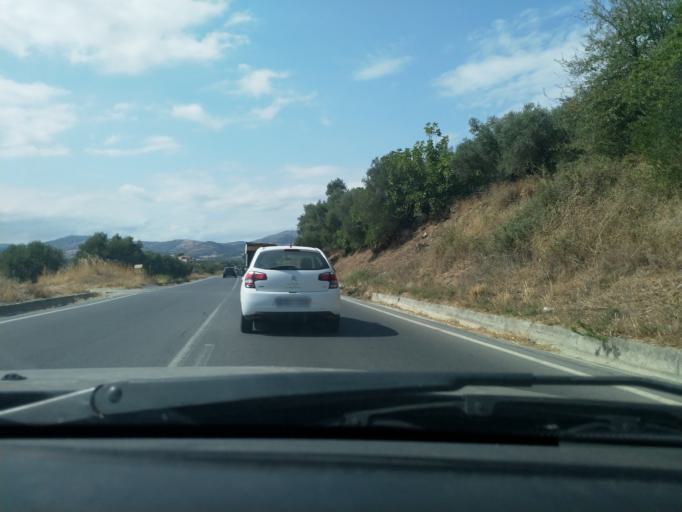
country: GR
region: Crete
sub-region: Nomos Rethymnis
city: Atsipopoulon
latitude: 35.2246
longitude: 24.4817
